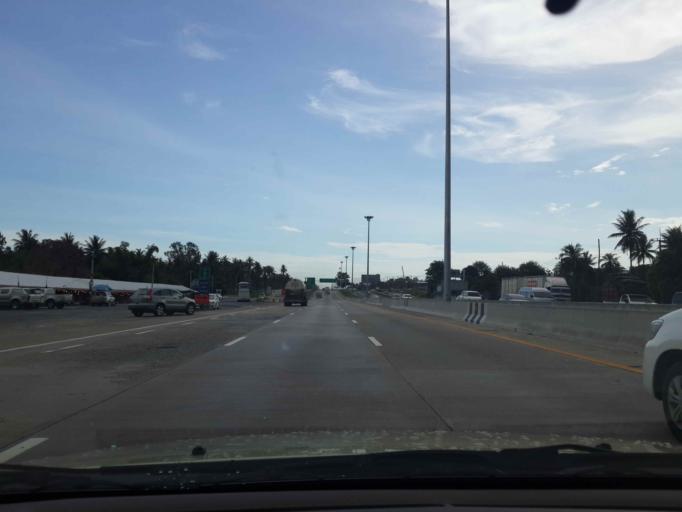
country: TH
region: Chon Buri
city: Bang Lamung
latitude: 12.9762
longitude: 100.9840
